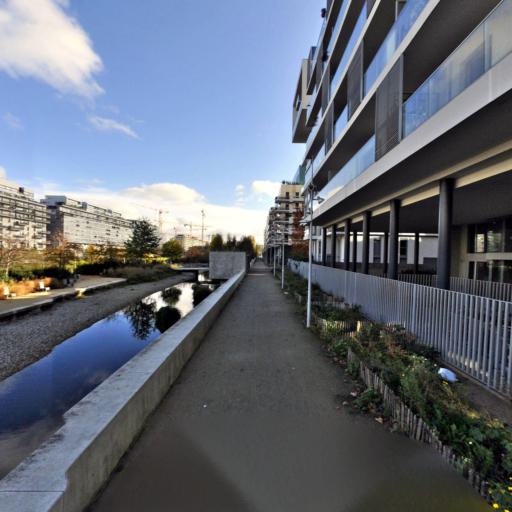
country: FR
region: Ile-de-France
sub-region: Departement des Hauts-de-Seine
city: Meudon
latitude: 48.8263
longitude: 2.2347
